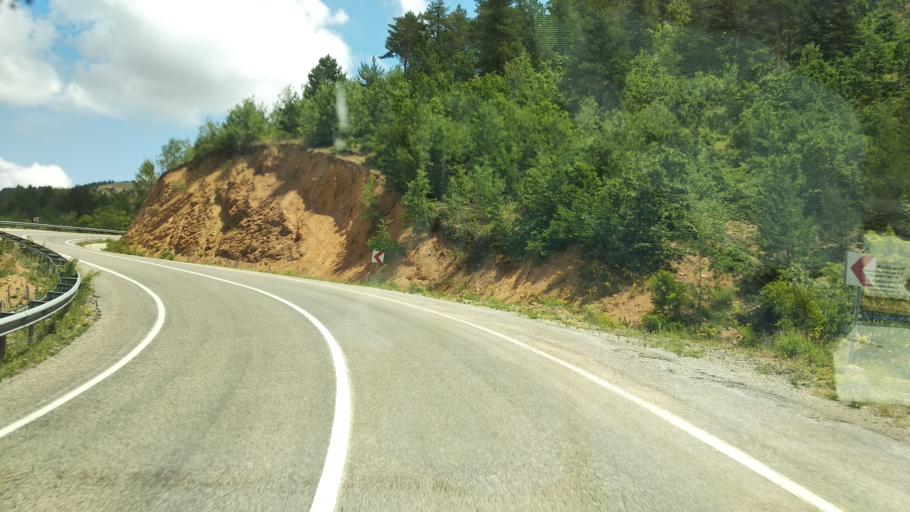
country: TR
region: Gumushane
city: Kose
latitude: 40.2982
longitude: 39.5611
